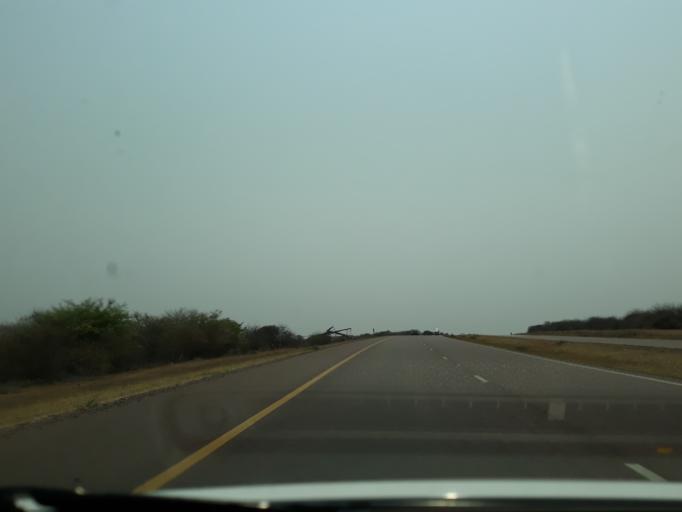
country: BW
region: Kgatleng
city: Bokaa
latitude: -24.4185
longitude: 26.0480
